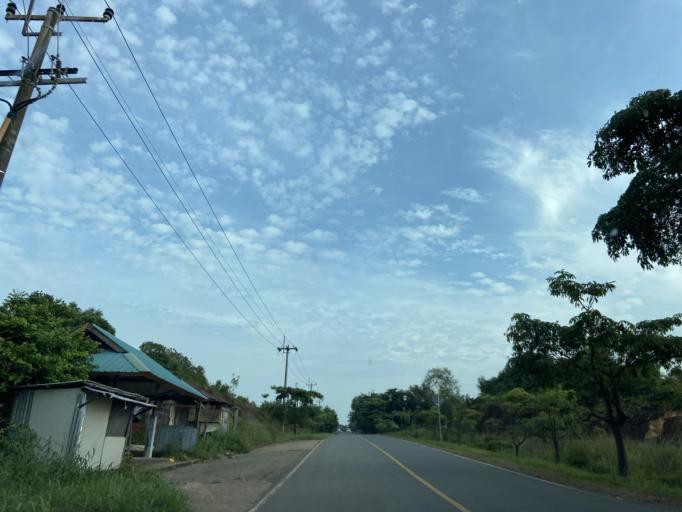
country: ID
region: Riau Islands
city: Tanjungpinang
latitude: 0.9232
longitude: 104.1166
